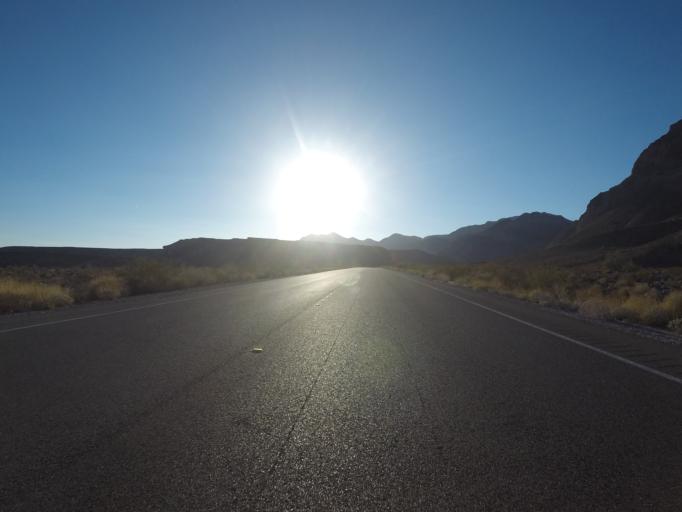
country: US
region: Nevada
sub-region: Clark County
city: Moapa Valley
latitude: 36.3649
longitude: -114.4639
